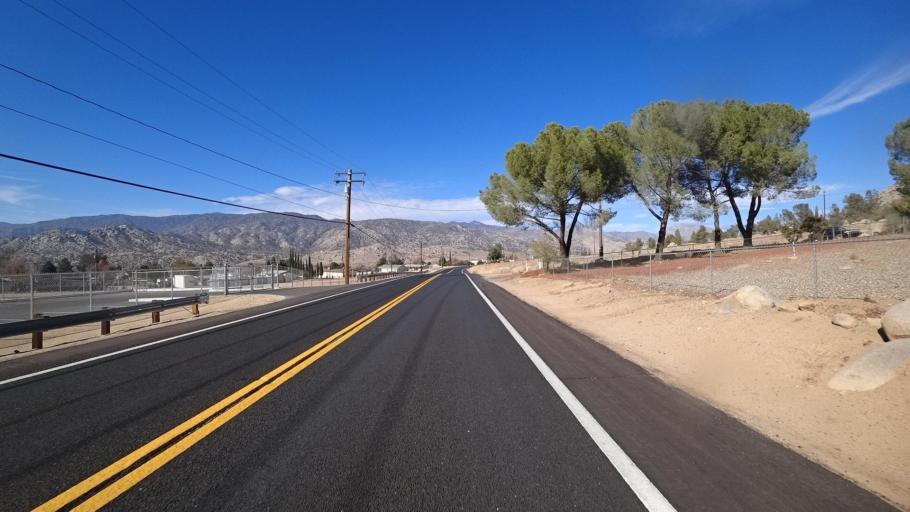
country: US
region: California
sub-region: Kern County
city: Lake Isabella
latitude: 35.6121
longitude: -118.4676
